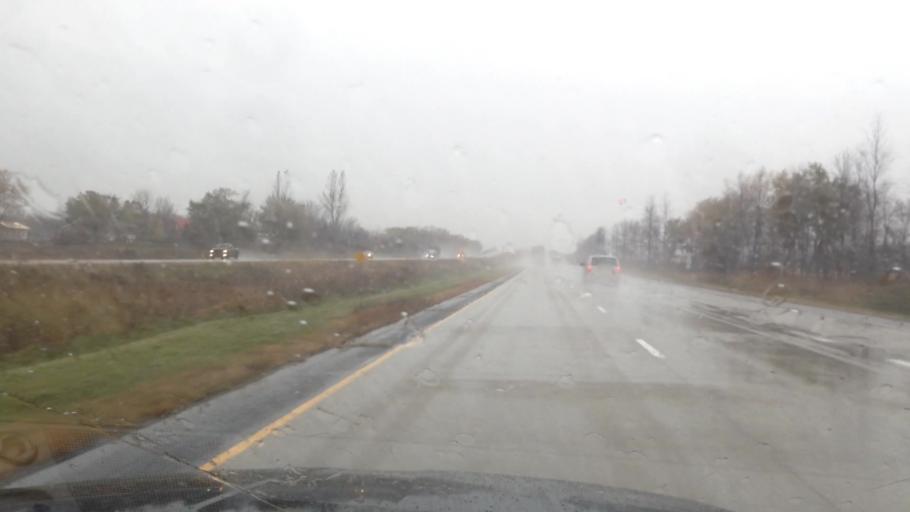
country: CA
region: Ontario
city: Hawkesbury
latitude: 45.5177
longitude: -74.5641
